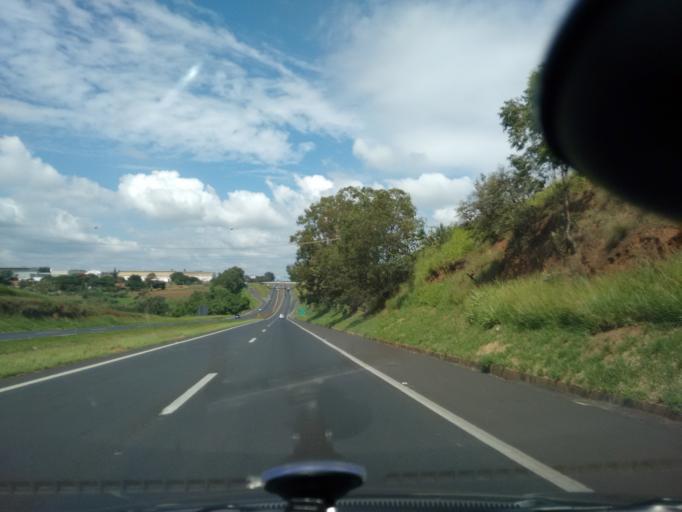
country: BR
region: Sao Paulo
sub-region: Sao Carlos
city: Sao Carlos
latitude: -22.0305
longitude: -47.8600
